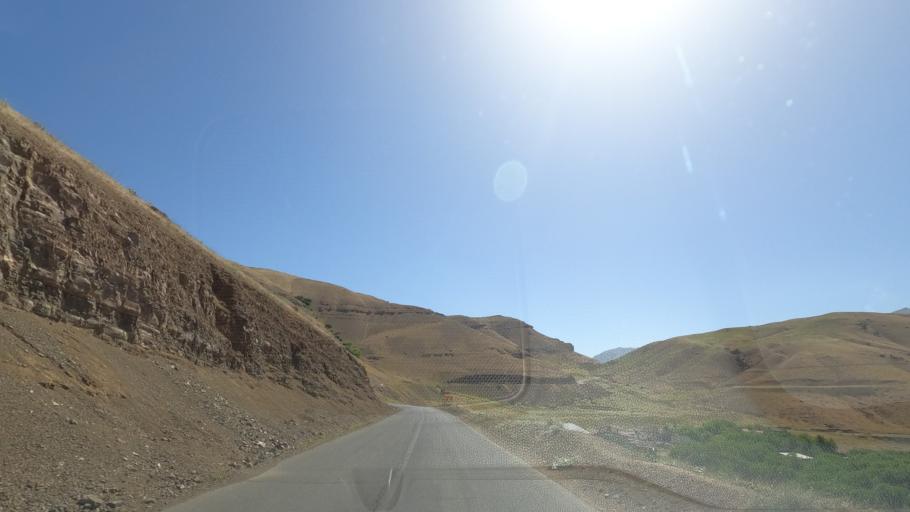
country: IR
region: Alborz
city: Karaj
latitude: 35.9264
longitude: 51.0911
